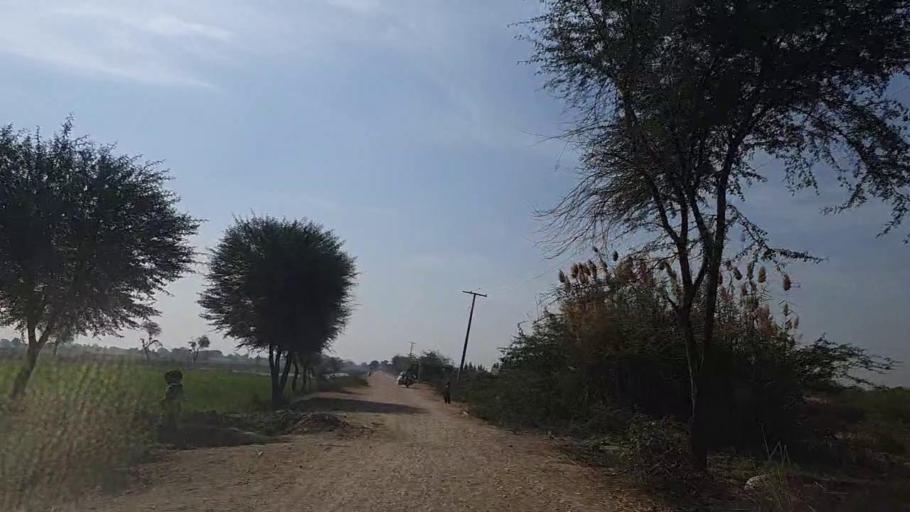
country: PK
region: Sindh
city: Mirpur Khas
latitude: 25.4798
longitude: 68.9745
